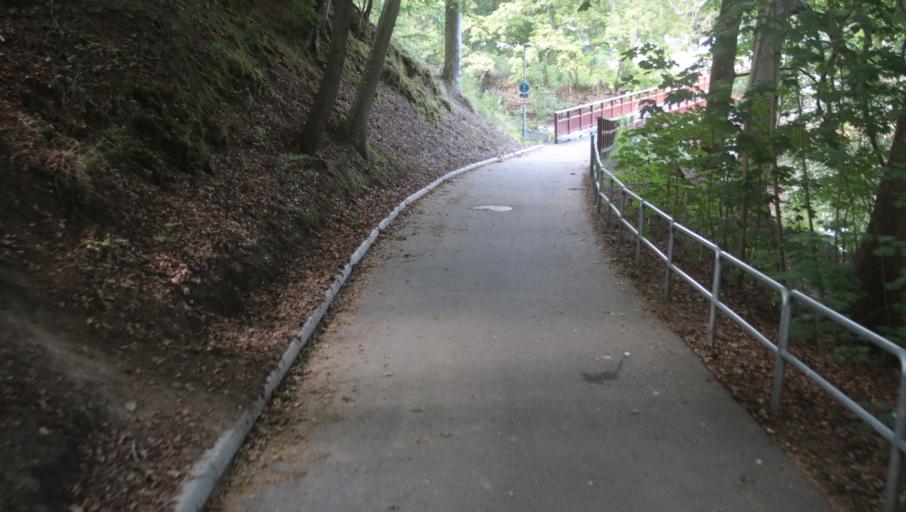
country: SE
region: Blekinge
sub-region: Karlshamns Kommun
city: Morrum
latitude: 56.2009
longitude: 14.7512
